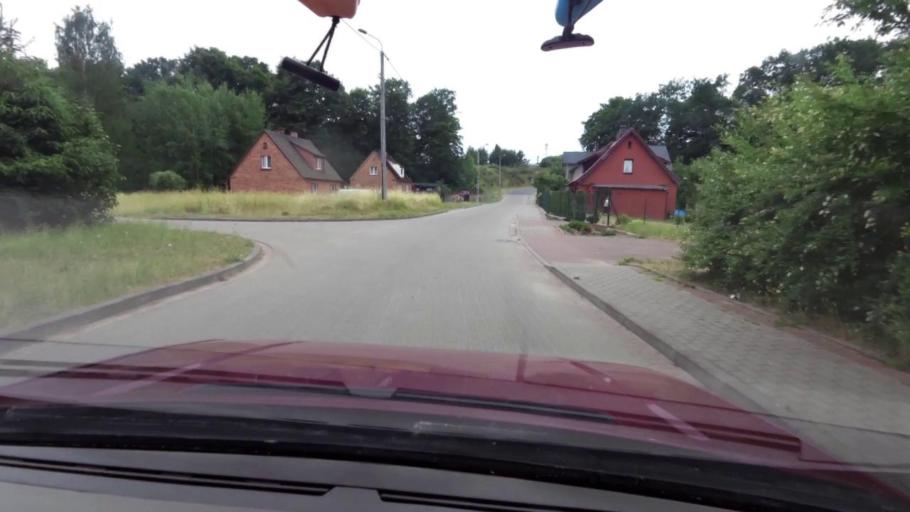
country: PL
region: Pomeranian Voivodeship
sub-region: Powiat slupski
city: Kepice
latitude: 54.2451
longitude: 16.8939
